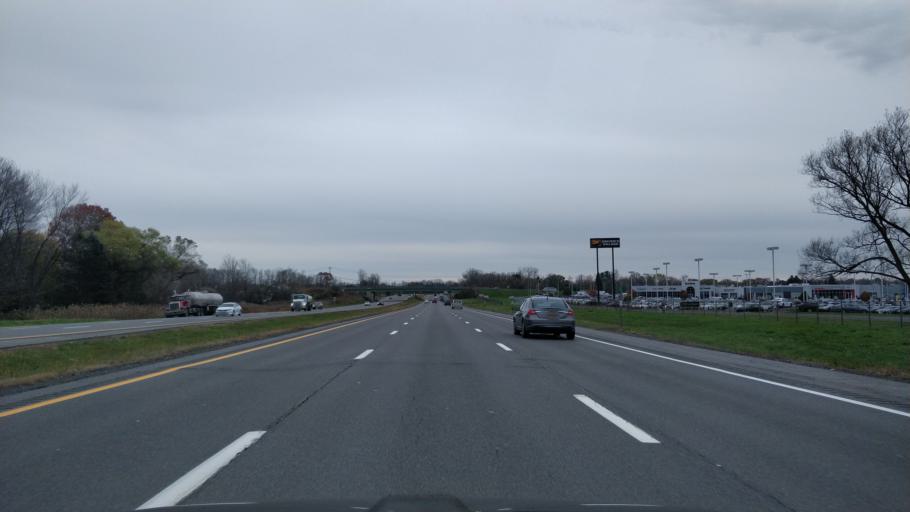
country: US
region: New York
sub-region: Onondaga County
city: North Syracuse
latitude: 43.1536
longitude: -76.1106
